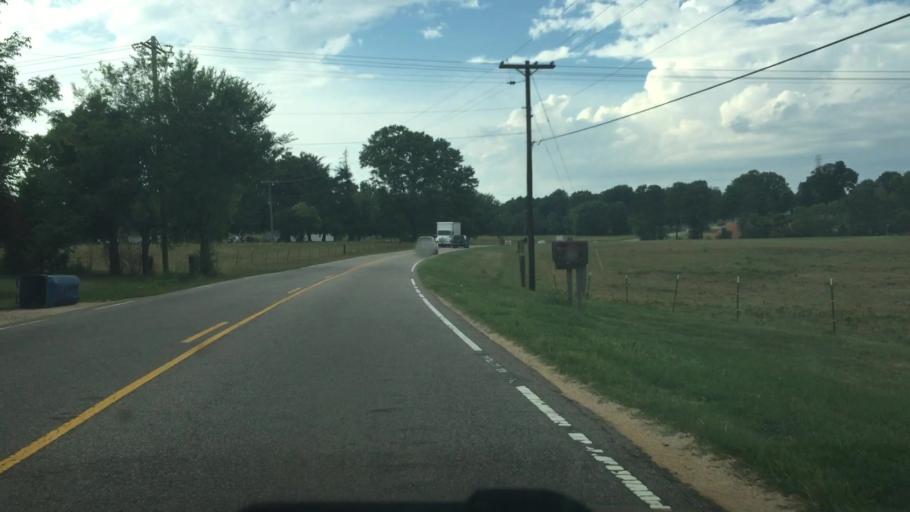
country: US
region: North Carolina
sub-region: Gaston County
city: Davidson
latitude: 35.4959
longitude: -80.7694
